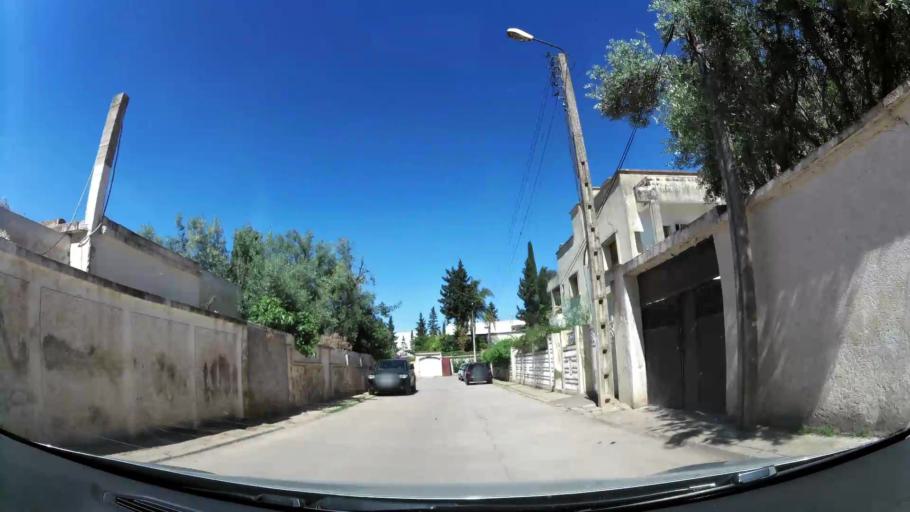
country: MA
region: Fes-Boulemane
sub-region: Fes
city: Fes
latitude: 34.0205
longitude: -4.9917
